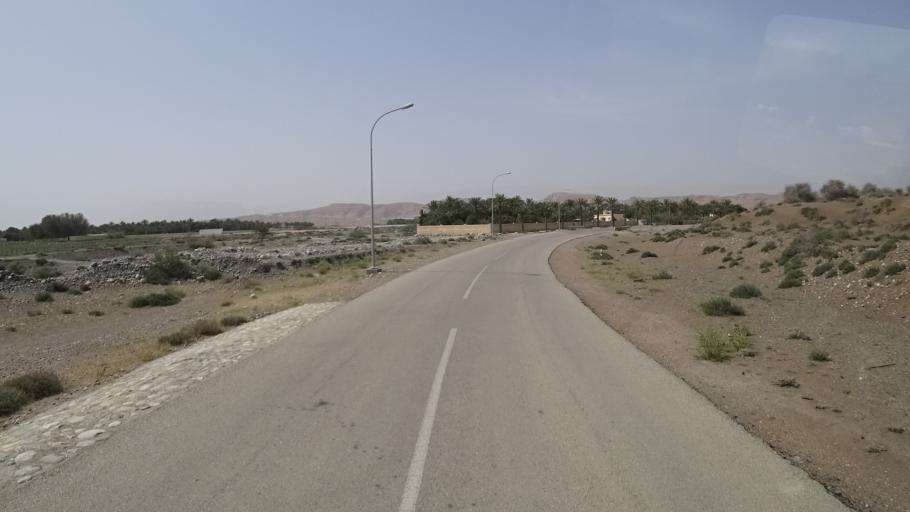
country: OM
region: Muhafazat Masqat
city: Muscat
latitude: 23.2103
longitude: 58.9733
